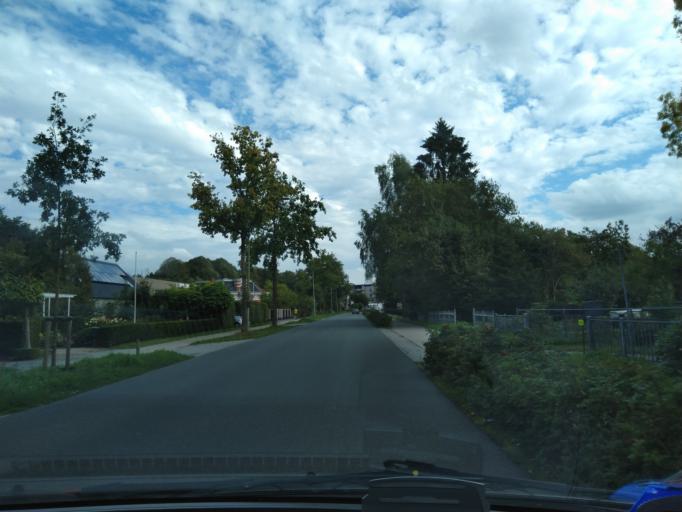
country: NL
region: Groningen
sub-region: Gemeente Haren
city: Haren
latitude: 53.1601
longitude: 6.5606
